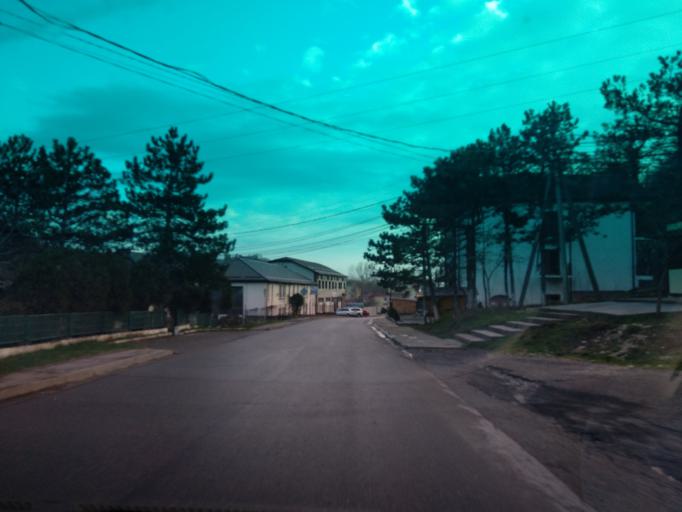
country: RU
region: Krasnodarskiy
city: Novomikhaylovskiy
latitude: 44.2627
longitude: 38.8231
